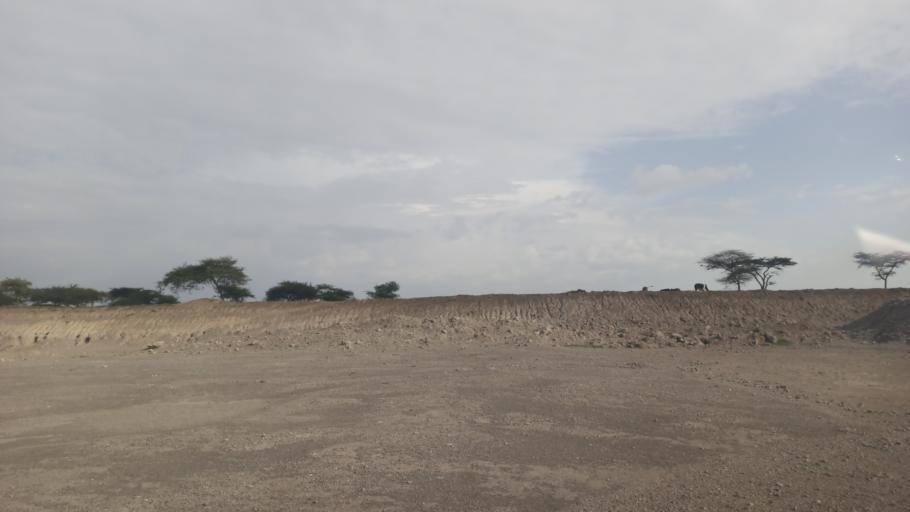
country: ET
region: Oromiya
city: Ziway
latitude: 7.6679
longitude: 38.6763
